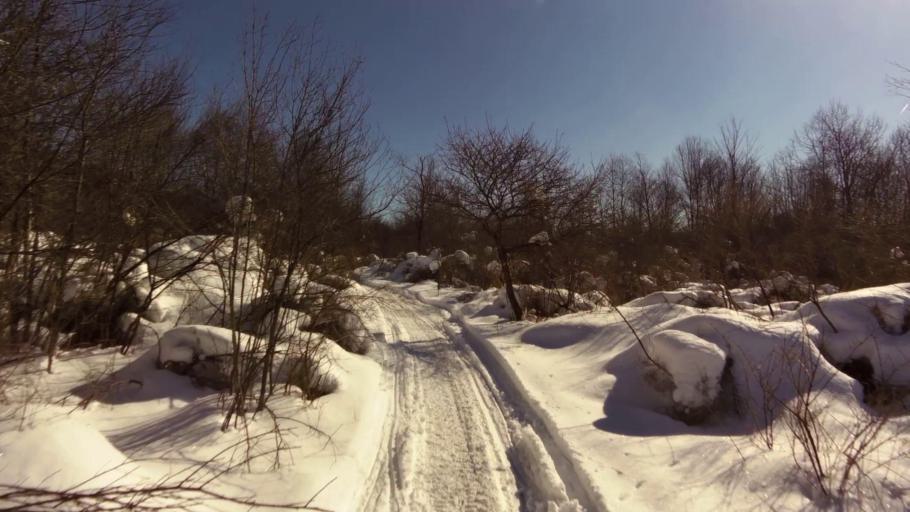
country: US
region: New York
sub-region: Cattaraugus County
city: Franklinville
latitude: 42.3472
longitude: -78.4325
